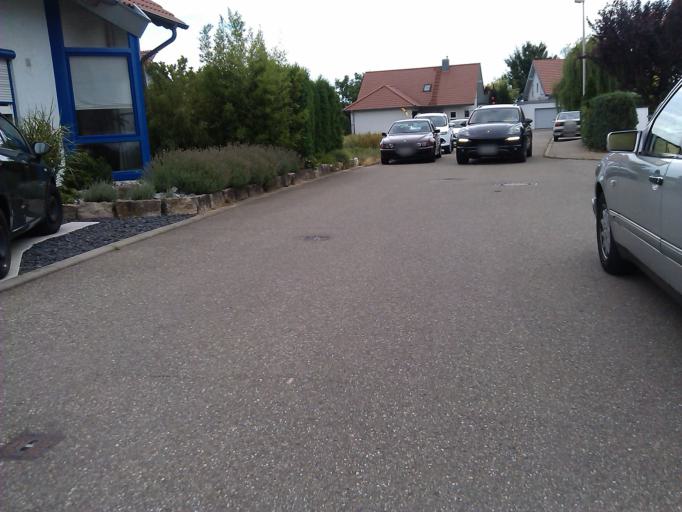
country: DE
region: Baden-Wuerttemberg
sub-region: Regierungsbezirk Stuttgart
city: Talheim
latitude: 49.0770
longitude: 9.1937
